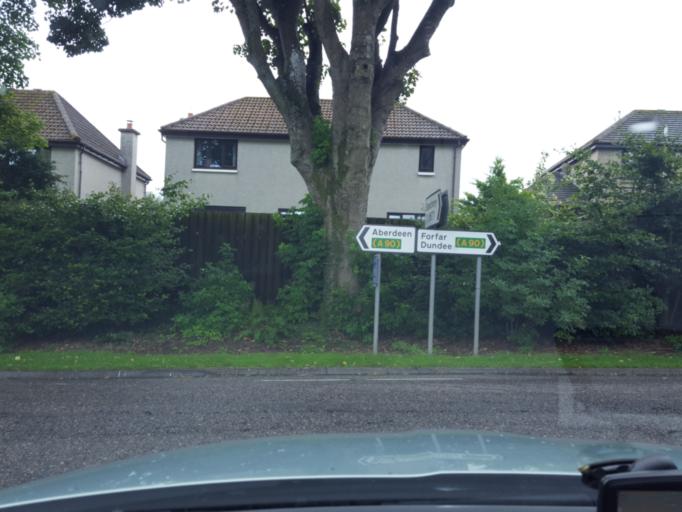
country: GB
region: Scotland
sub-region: Aberdeenshire
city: Stonehaven
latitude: 56.9673
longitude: -2.2358
